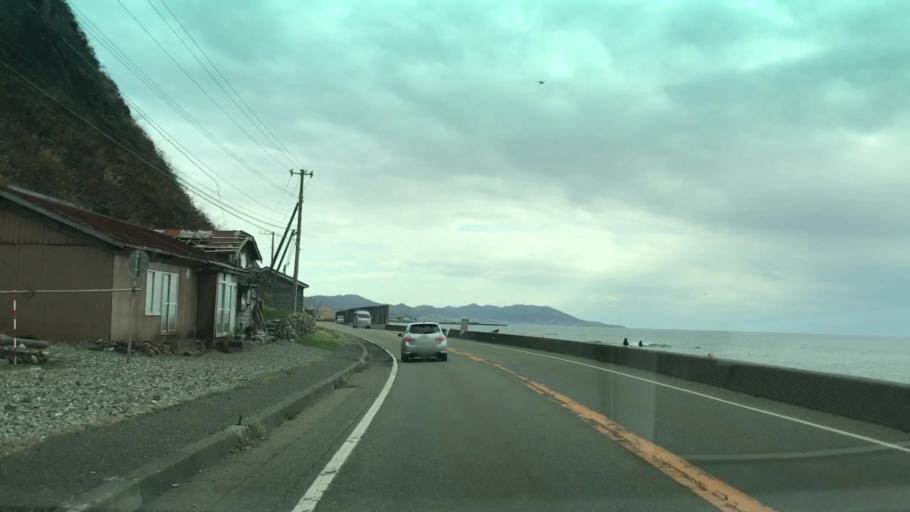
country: JP
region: Hokkaido
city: Shizunai-furukawacho
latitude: 42.0546
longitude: 143.0837
